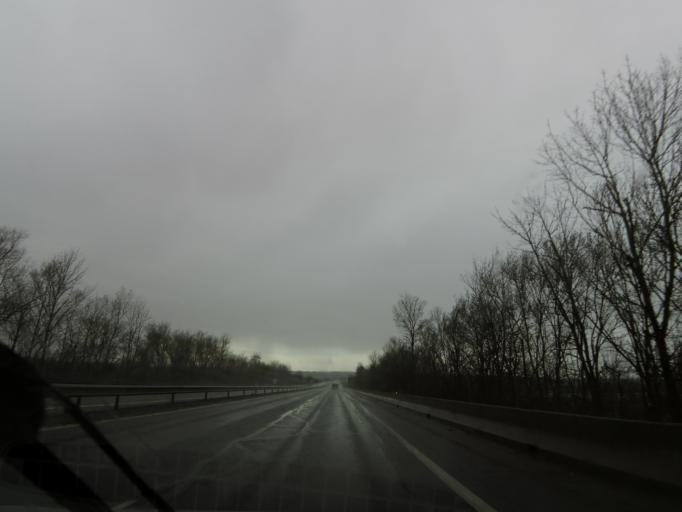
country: FR
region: Rhone-Alpes
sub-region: Departement de l'Ain
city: Feillens
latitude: 46.3368
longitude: 4.8630
